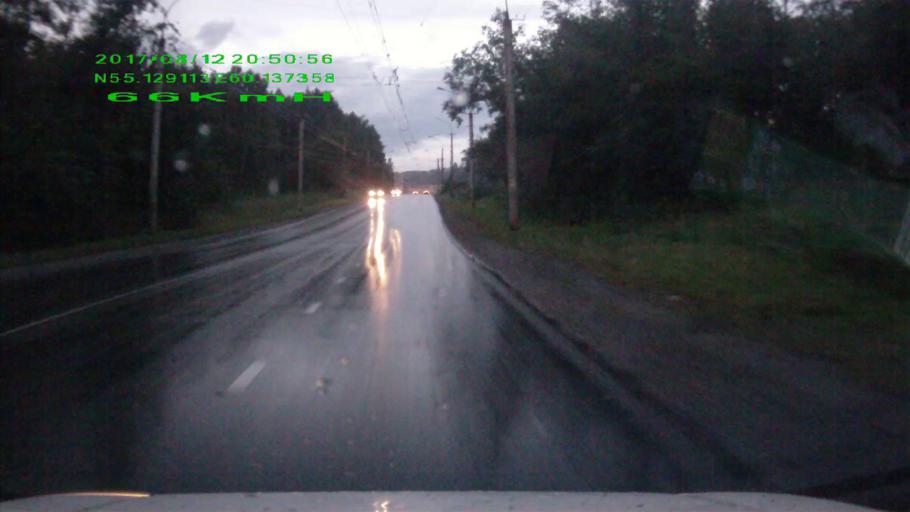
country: RU
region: Chelyabinsk
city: Turgoyak
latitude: 55.1291
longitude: 60.1374
